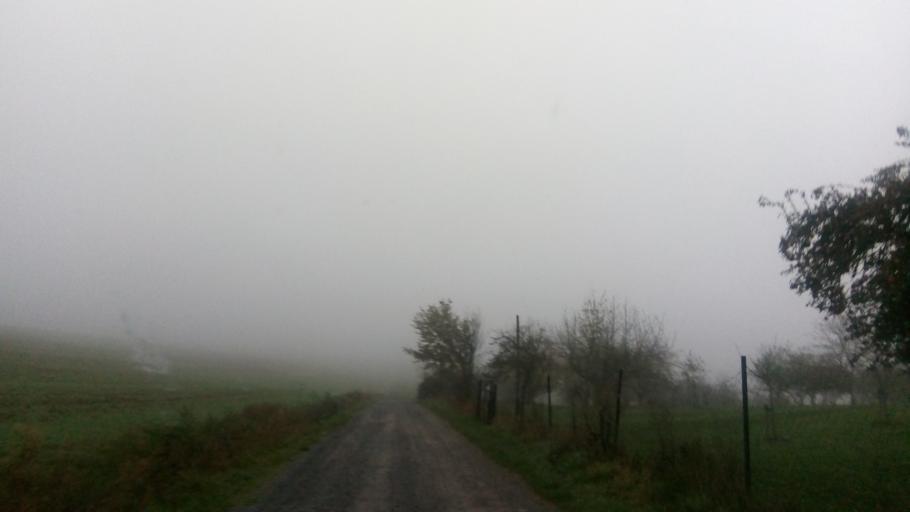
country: DE
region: Bavaria
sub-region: Regierungsbezirk Unterfranken
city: Dittelbrunn
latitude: 50.0963
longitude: 10.2381
